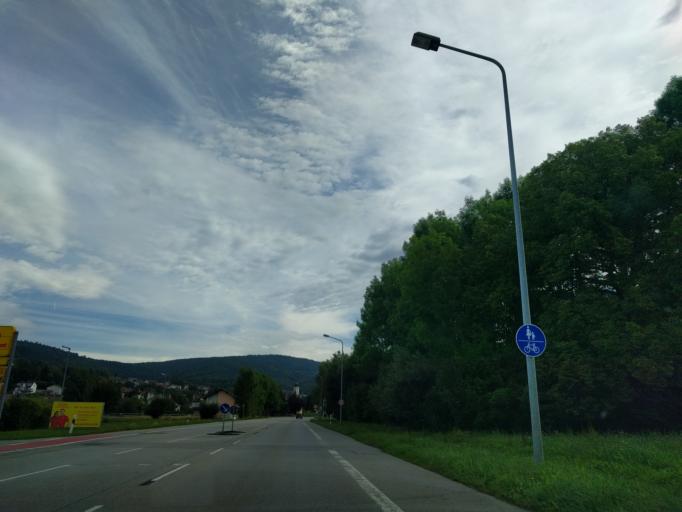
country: DE
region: Bavaria
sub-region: Lower Bavaria
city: Deggendorf
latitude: 48.8512
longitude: 12.9884
